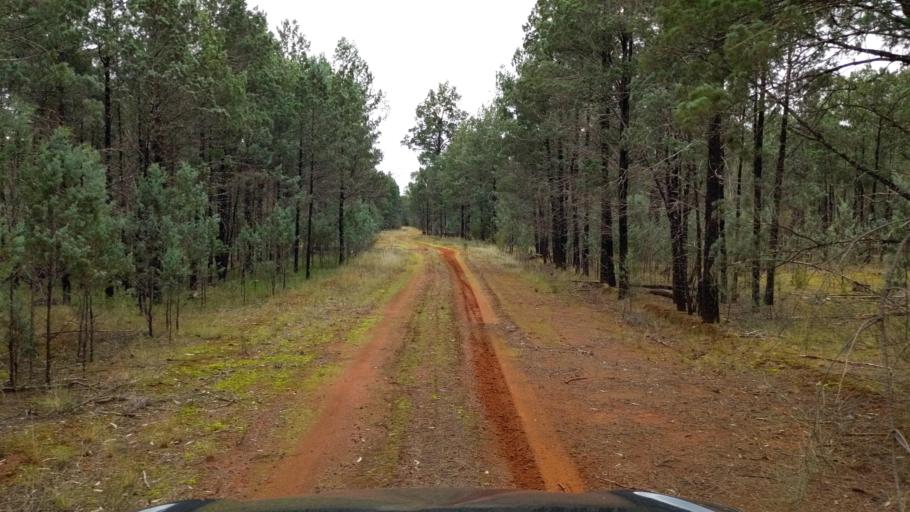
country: AU
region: New South Wales
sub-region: Coolamon
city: Coolamon
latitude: -34.8479
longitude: 146.9323
